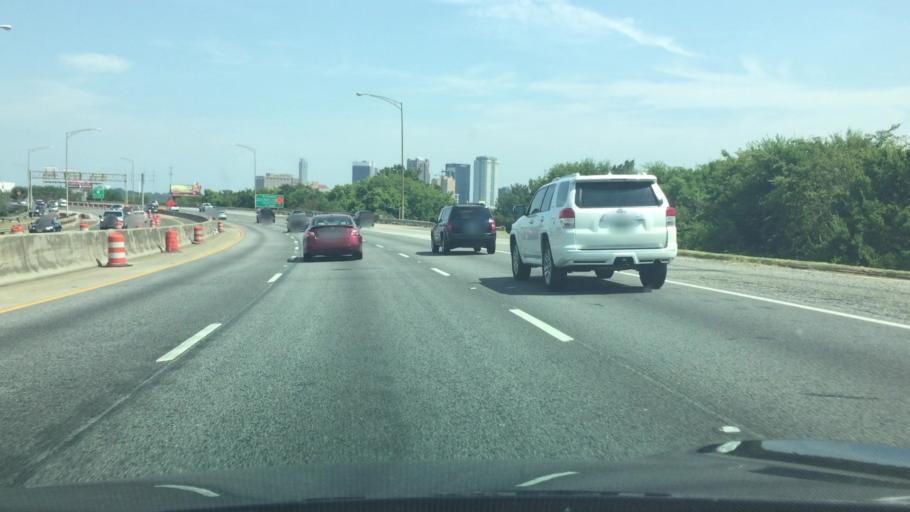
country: US
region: Alabama
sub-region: Jefferson County
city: Birmingham
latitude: 33.4994
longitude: -86.8142
